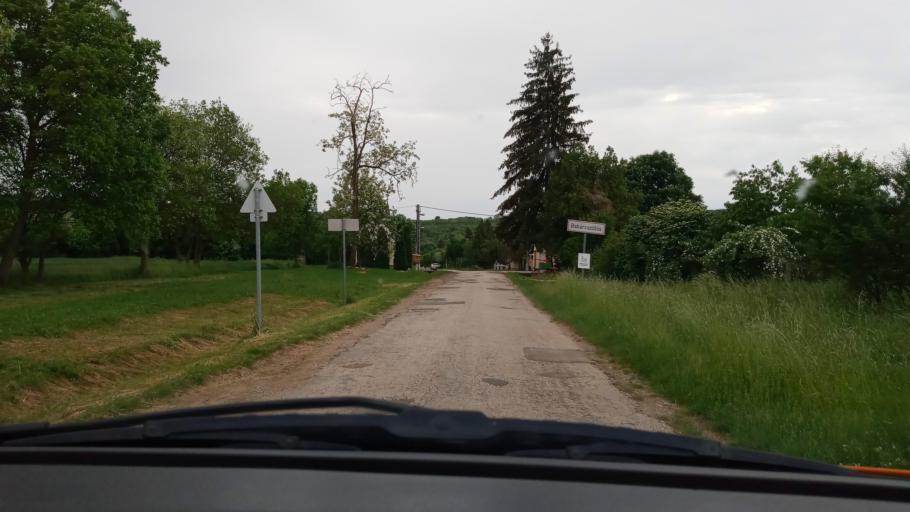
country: HU
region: Baranya
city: Harkany
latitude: 45.9009
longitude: 18.1370
